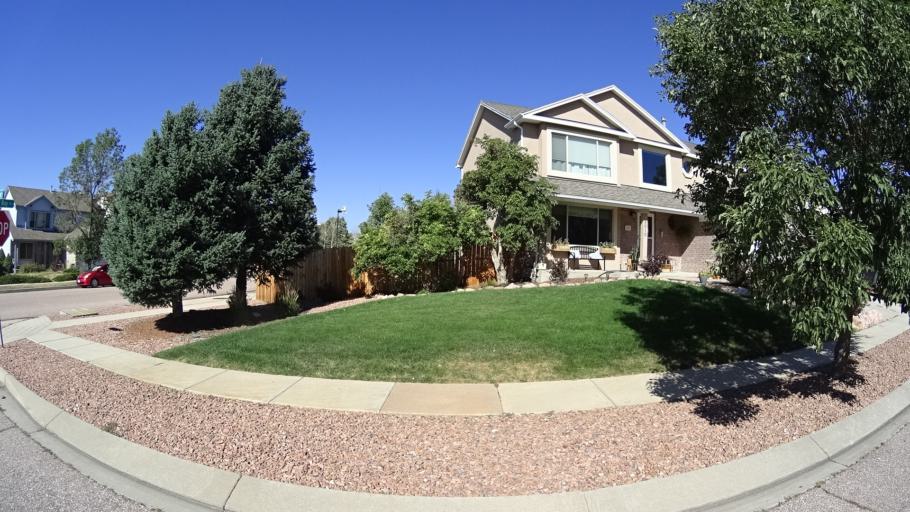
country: US
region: Colorado
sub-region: El Paso County
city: Black Forest
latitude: 38.9474
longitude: -104.7321
